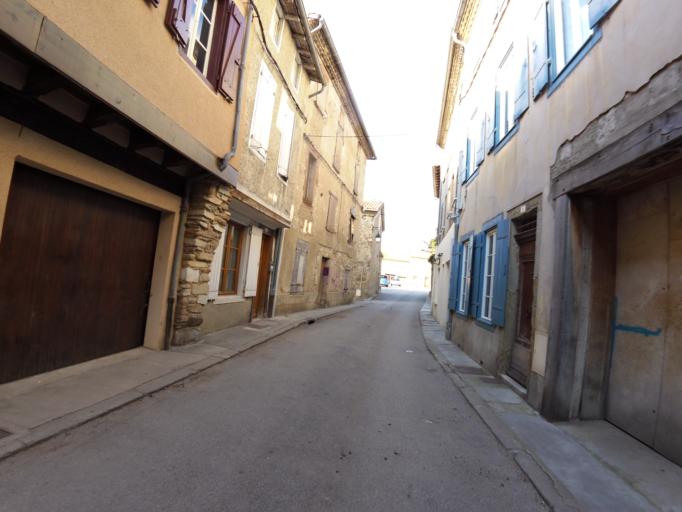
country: FR
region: Midi-Pyrenees
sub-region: Departement du Tarn
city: Soreze
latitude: 43.4530
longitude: 2.0684
